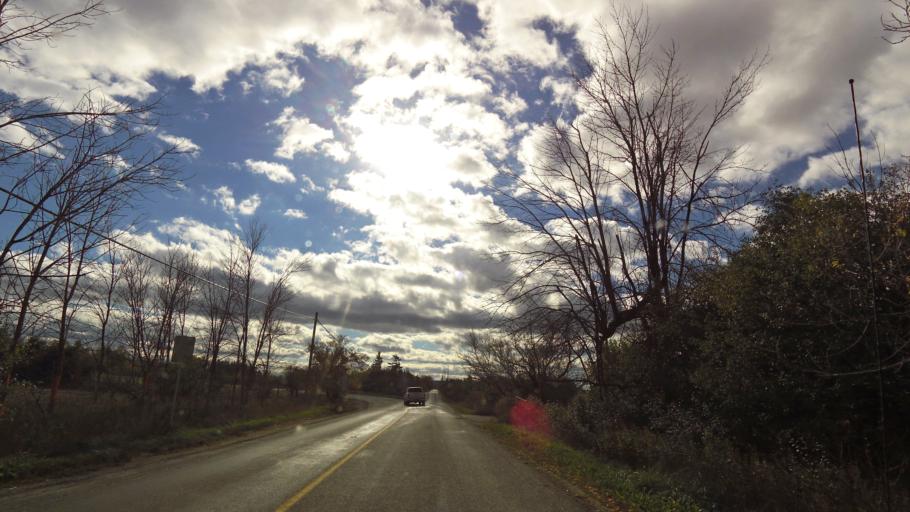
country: CA
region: Ontario
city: Burlington
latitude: 43.4641
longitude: -79.8110
